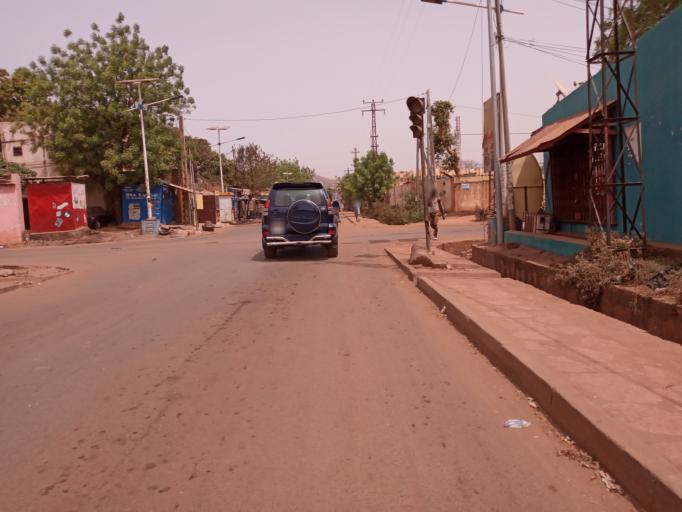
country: ML
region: Bamako
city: Bamako
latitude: 12.6465
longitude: -7.9802
